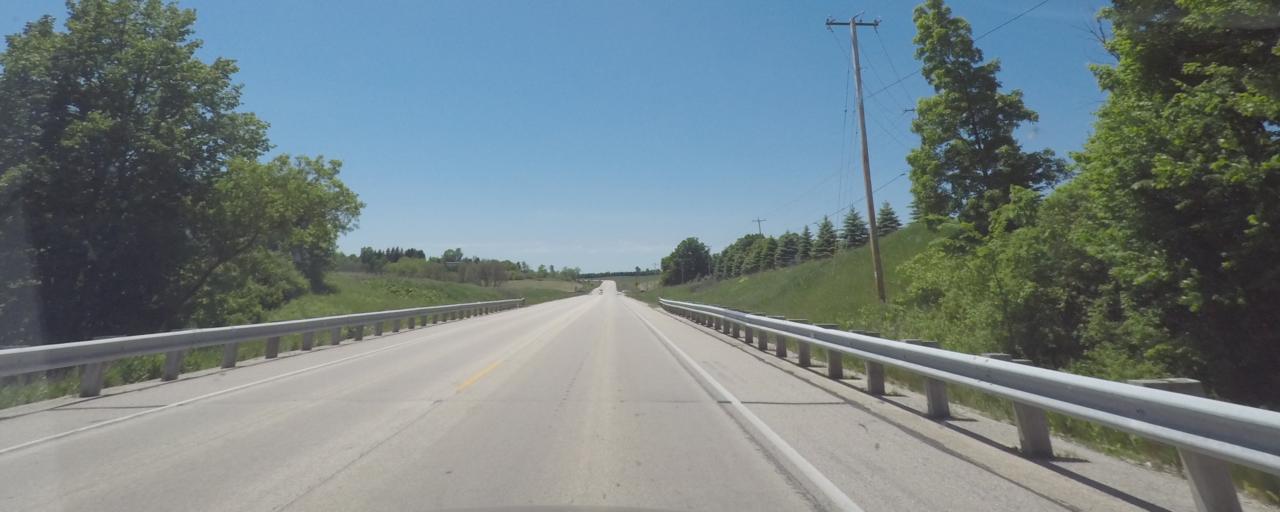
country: US
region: Wisconsin
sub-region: Washington County
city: West Bend
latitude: 43.5014
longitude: -88.1328
